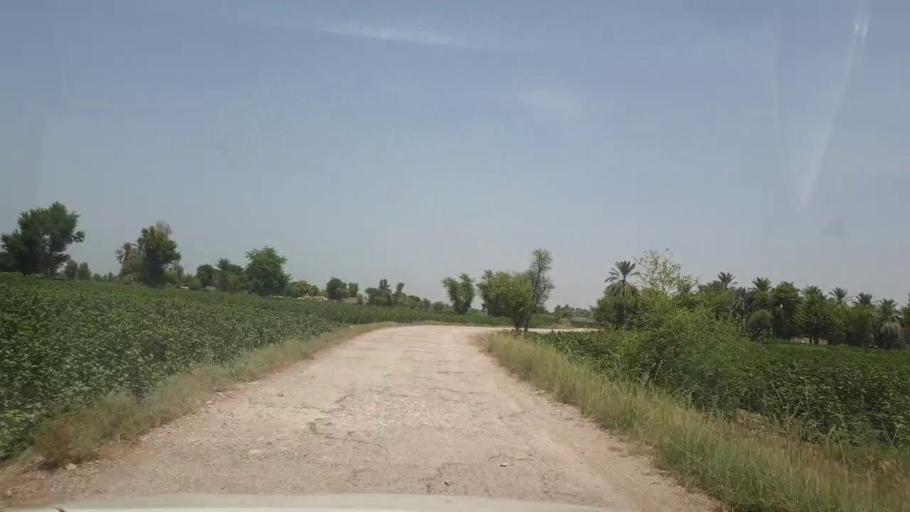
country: PK
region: Sindh
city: Bozdar
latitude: 27.1670
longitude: 68.6219
